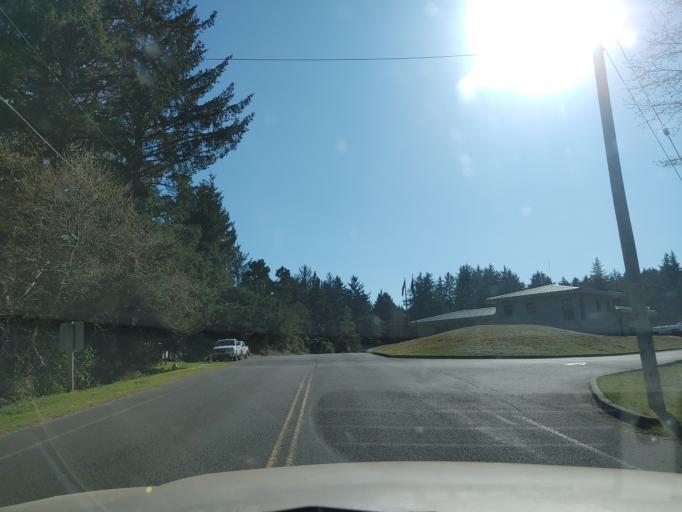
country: US
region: Oregon
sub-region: Clatsop County
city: Warrenton
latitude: 46.1828
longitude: -123.9609
